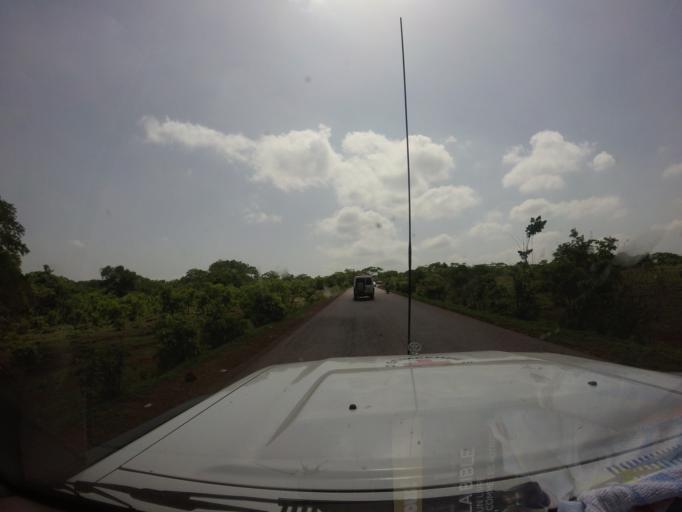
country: GN
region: Mamou
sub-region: Mamou Prefecture
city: Mamou
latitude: 10.2915
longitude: -12.3564
